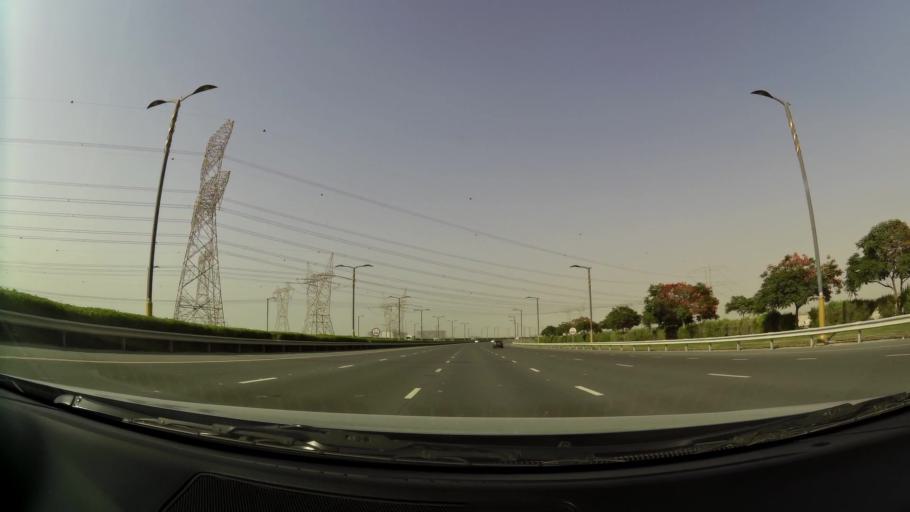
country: AE
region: Dubai
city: Dubai
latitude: 25.1680
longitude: 55.3041
